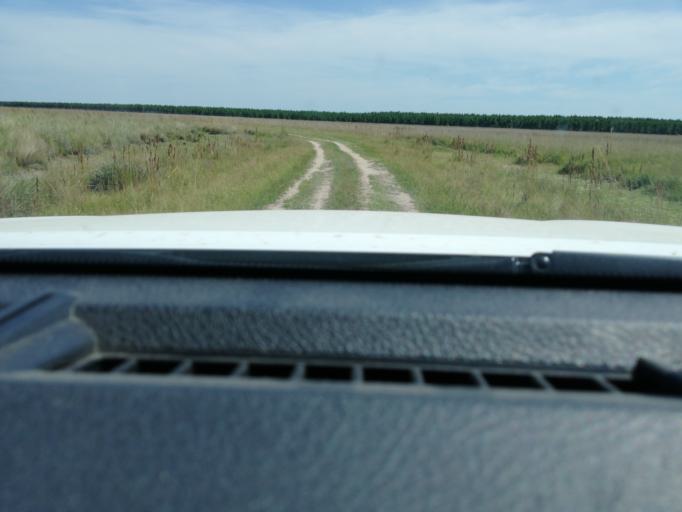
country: AR
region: Corrientes
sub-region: Departamento de San Miguel
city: San Miguel
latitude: -28.0464
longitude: -57.4557
